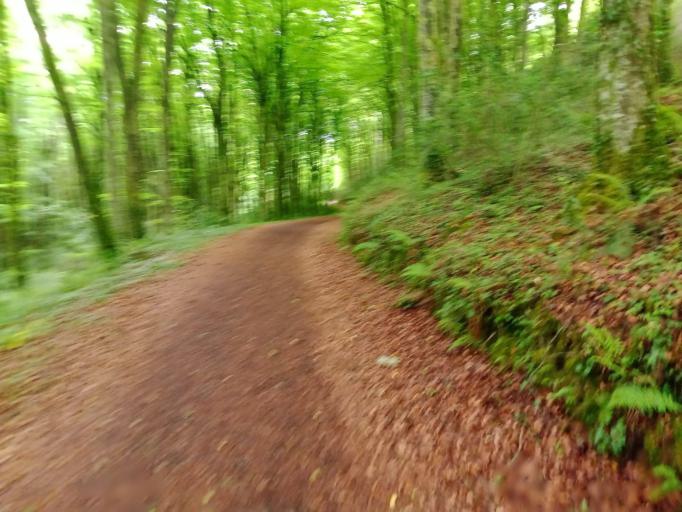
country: IE
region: Leinster
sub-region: Laois
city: Stradbally
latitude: 53.0015
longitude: -7.1185
